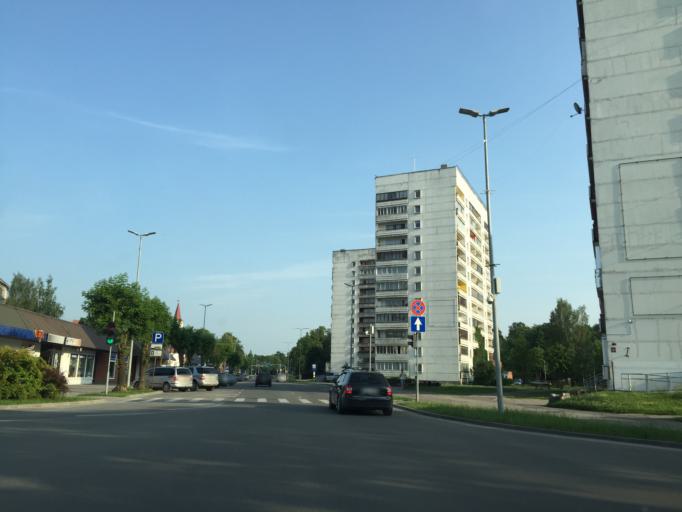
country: LV
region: Jelgava
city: Jelgava
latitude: 56.6468
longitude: 23.7259
